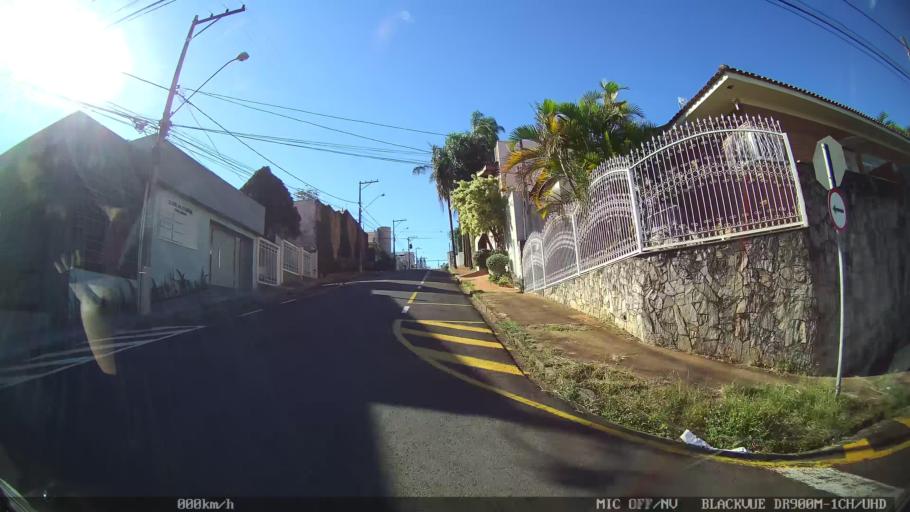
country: BR
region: Sao Paulo
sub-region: Franca
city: Franca
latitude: -20.5394
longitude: -47.4063
